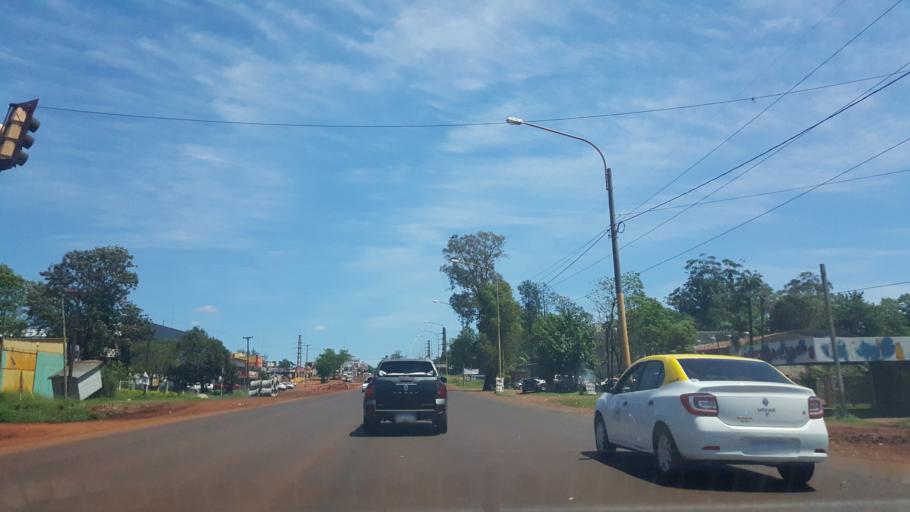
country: AR
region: Misiones
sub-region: Departamento de Capital
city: Posadas
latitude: -27.4028
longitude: -55.9177
